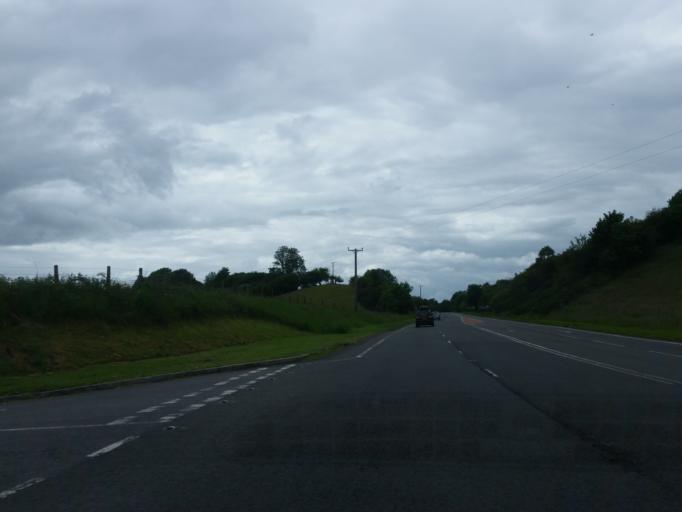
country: GB
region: Northern Ireland
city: Fivemiletown
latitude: 54.3816
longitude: -7.2712
